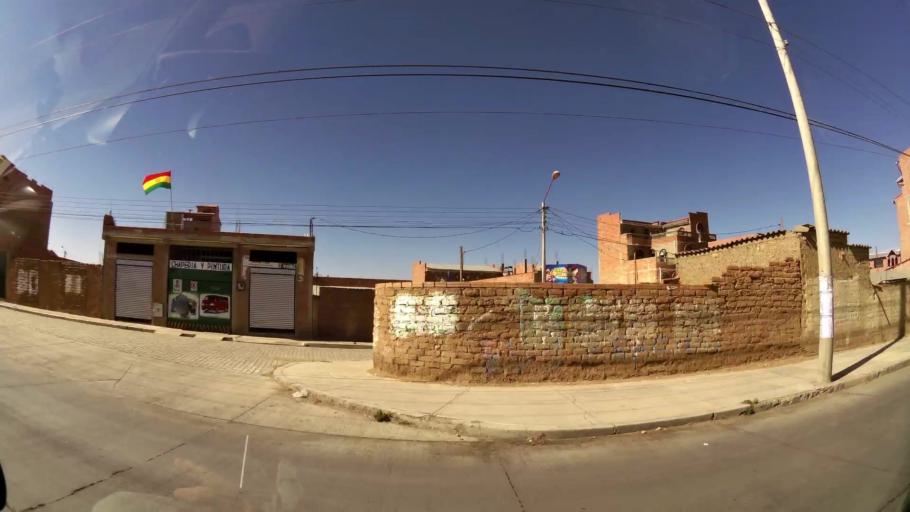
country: BO
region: La Paz
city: La Paz
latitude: -16.5225
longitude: -68.1936
